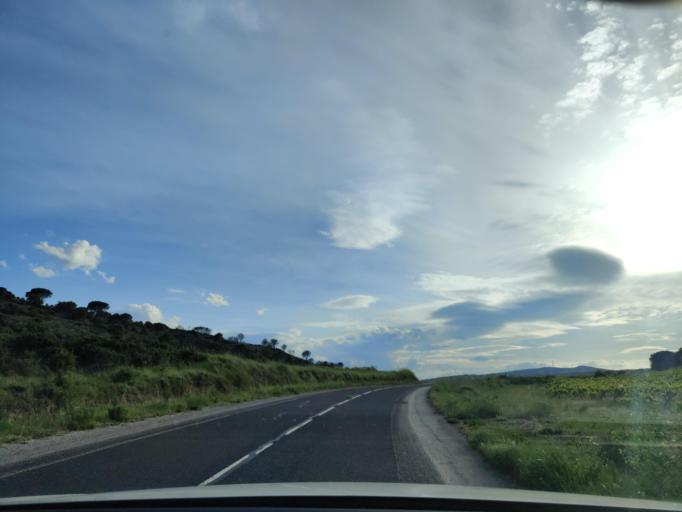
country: FR
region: Languedoc-Roussillon
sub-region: Departement des Pyrenees-Orientales
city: Estagel
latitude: 42.7904
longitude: 2.6933
